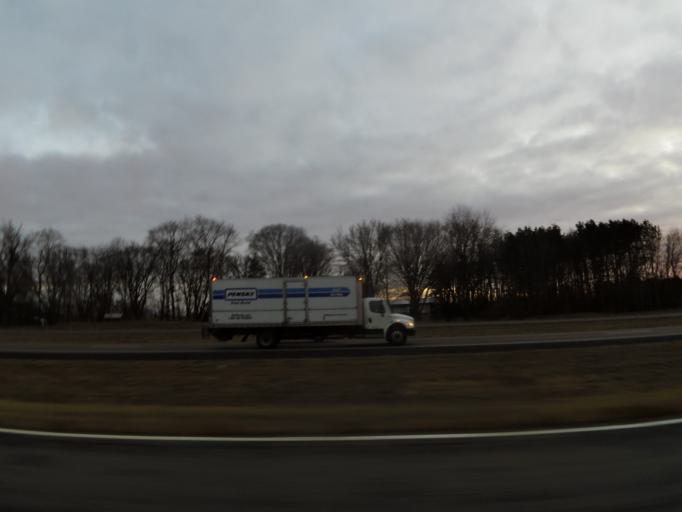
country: US
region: Minnesota
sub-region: Washington County
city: Lake Elmo
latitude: 45.0361
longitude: -92.8737
